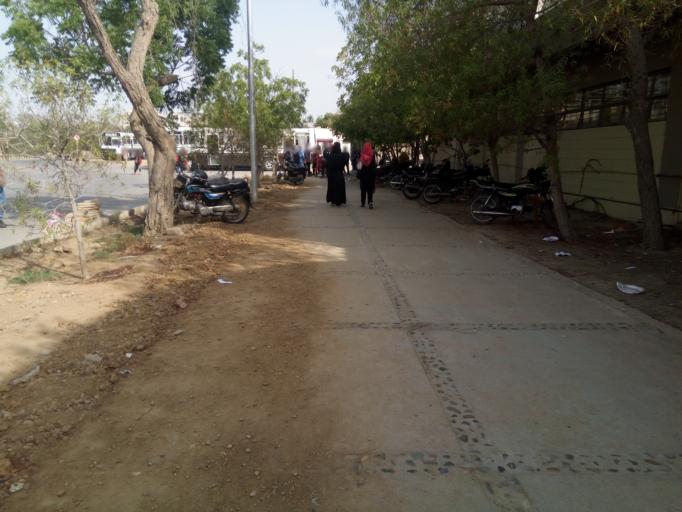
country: PK
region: Sindh
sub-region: Karachi District
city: Karachi
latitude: 24.9327
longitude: 67.1133
